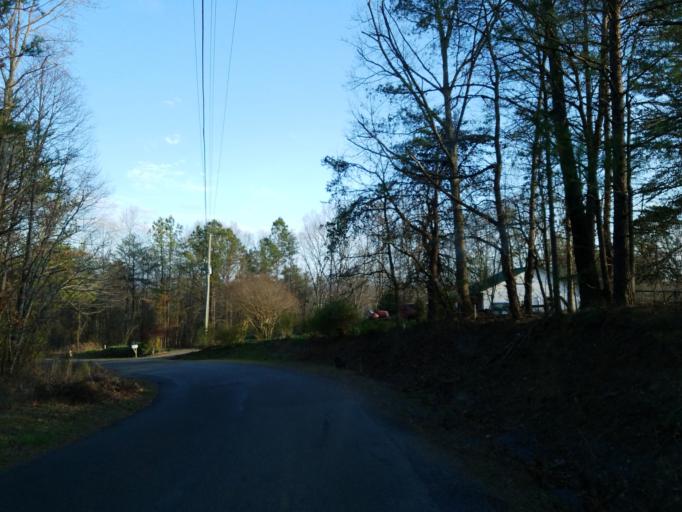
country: US
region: Georgia
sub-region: Pickens County
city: Jasper
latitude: 34.5105
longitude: -84.6114
